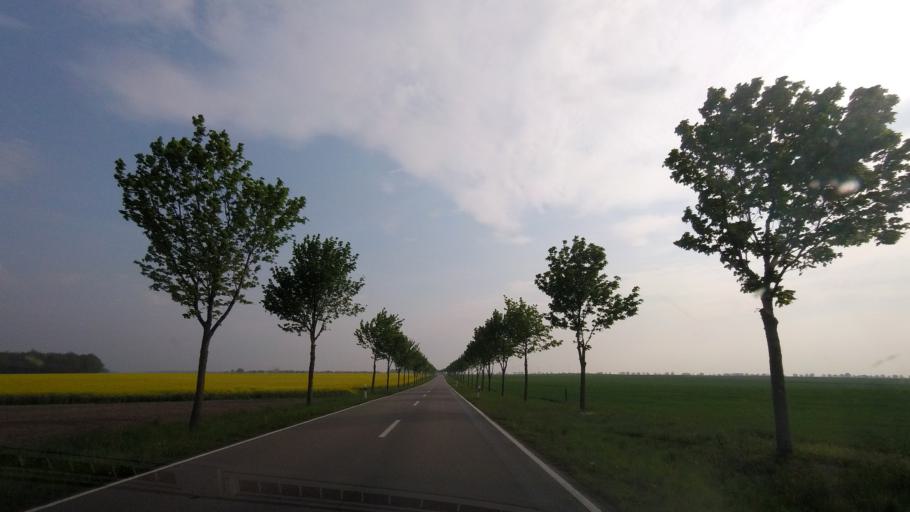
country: DE
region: Brandenburg
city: Juterbog
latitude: 51.9191
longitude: 13.1023
